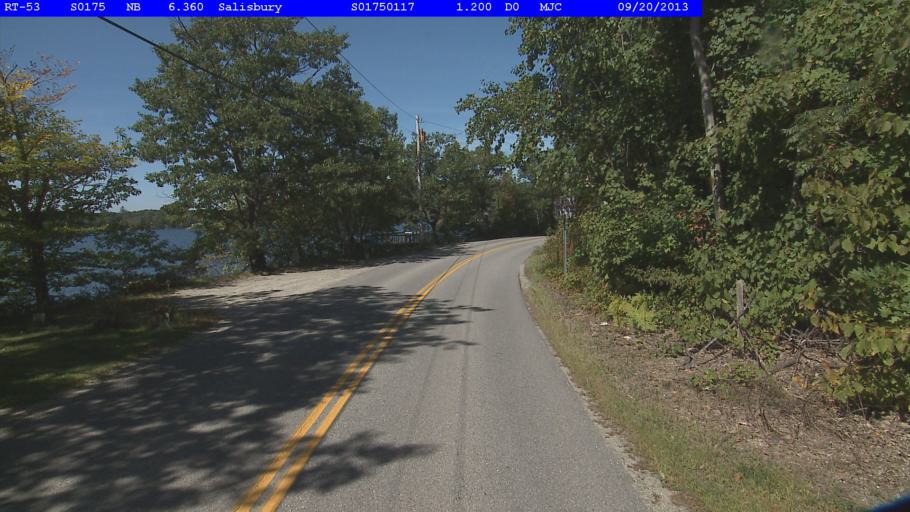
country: US
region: Vermont
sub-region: Rutland County
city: Brandon
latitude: 43.9146
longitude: -73.0683
